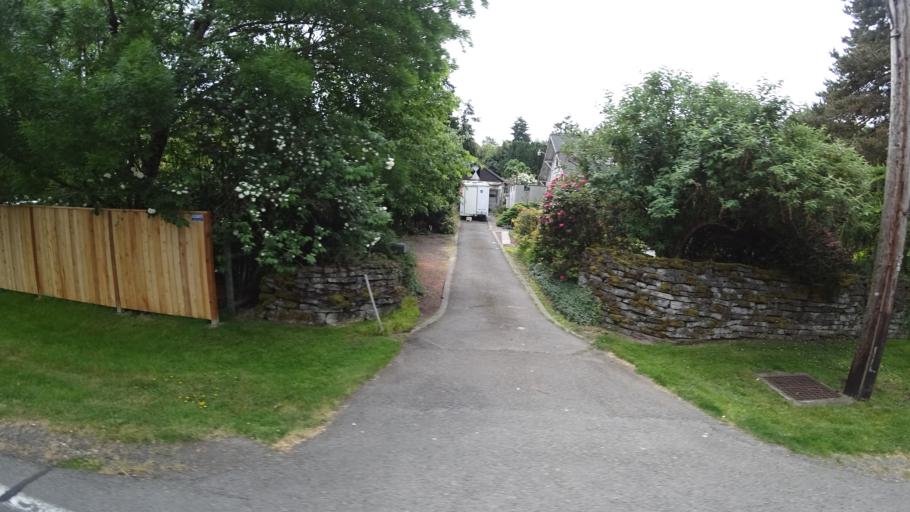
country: US
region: Oregon
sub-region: Clackamas County
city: Lake Oswego
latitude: 45.4635
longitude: -122.6941
